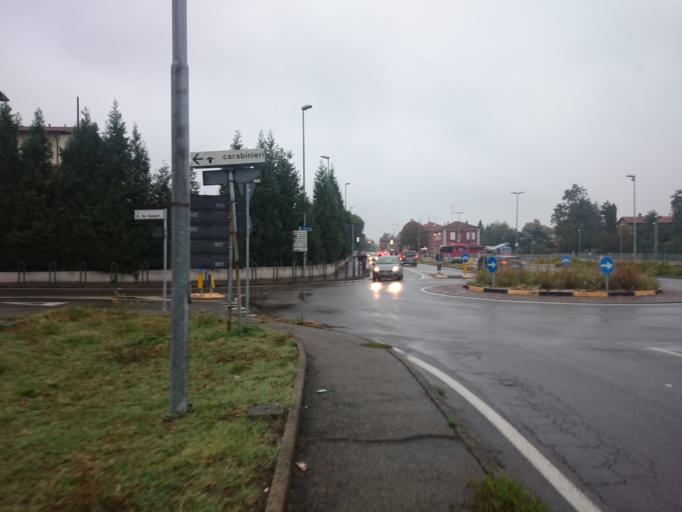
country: IT
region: Emilia-Romagna
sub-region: Provincia di Reggio Emilia
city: Scandiano
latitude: 44.5994
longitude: 10.6952
